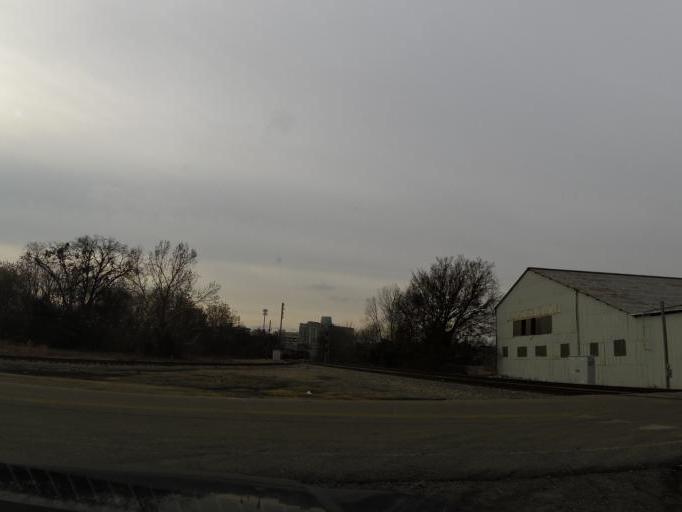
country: US
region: Alabama
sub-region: Montgomery County
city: Montgomery
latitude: 32.3856
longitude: -86.3112
